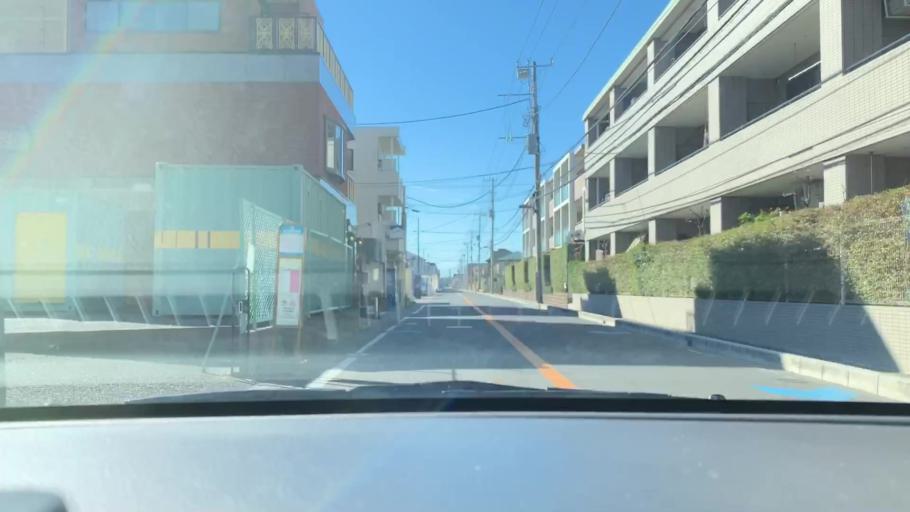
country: JP
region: Tokyo
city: Urayasu
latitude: 35.6491
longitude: 139.8981
